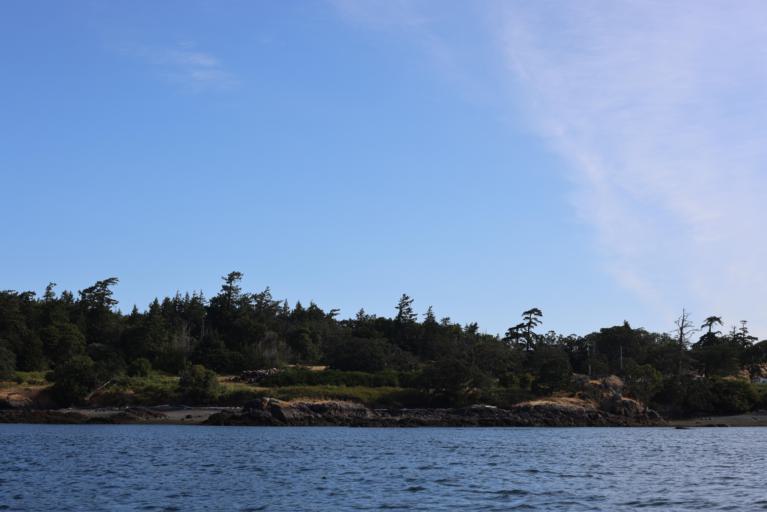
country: CA
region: British Columbia
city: Metchosin
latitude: 48.3373
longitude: -123.5452
